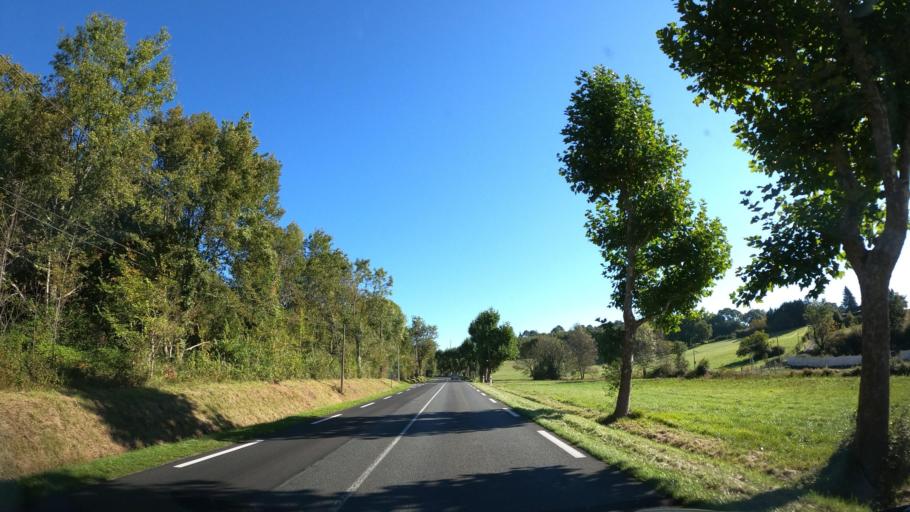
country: FR
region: Aquitaine
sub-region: Departement de la Dordogne
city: Lembras
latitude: 44.9454
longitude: 0.5723
